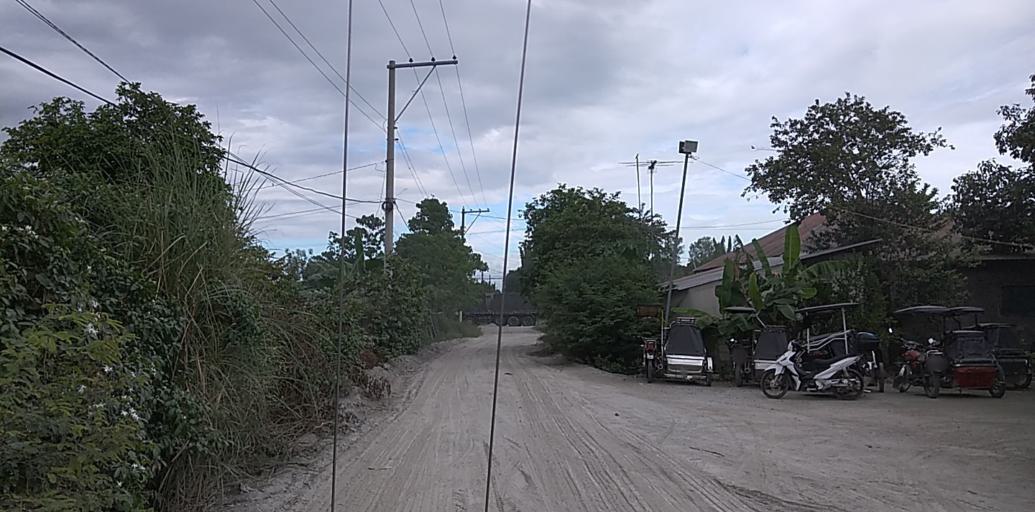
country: PH
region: Central Luzon
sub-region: Province of Pampanga
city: Pulung Santol
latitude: 15.0370
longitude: 120.5638
